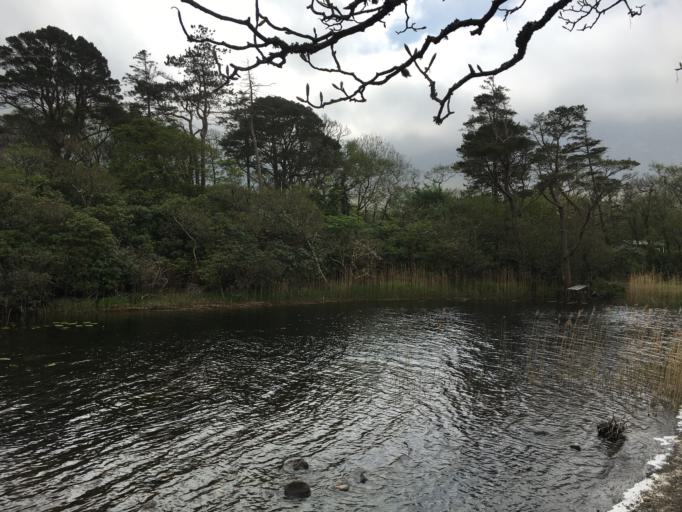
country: IE
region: Connaught
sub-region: County Galway
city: Clifden
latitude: 53.5603
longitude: -9.8908
